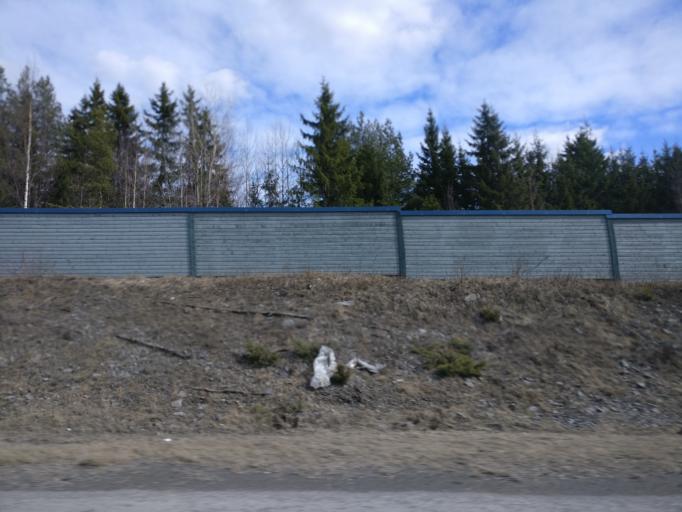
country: FI
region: Pirkanmaa
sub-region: Tampere
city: Lempaeaelae
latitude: 61.3782
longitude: 23.7912
